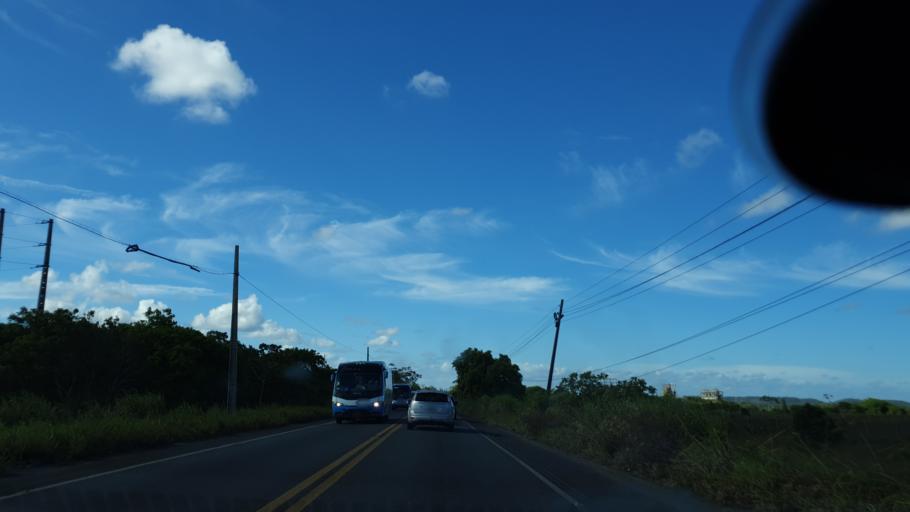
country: BR
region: Bahia
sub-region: Camacari
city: Camacari
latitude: -12.6649
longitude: -38.3012
